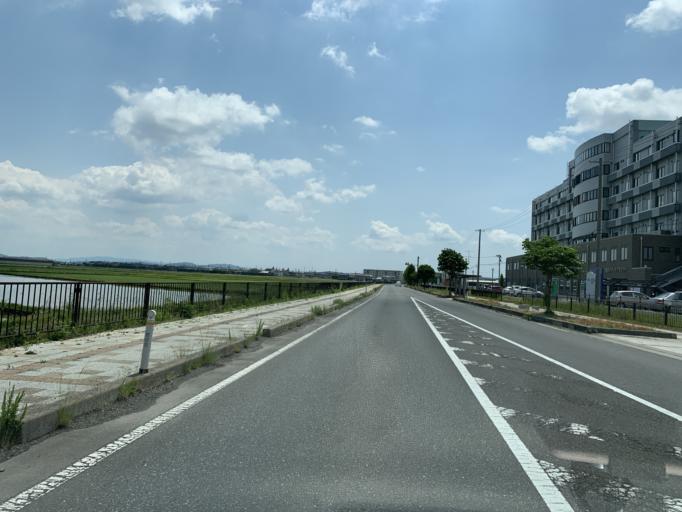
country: JP
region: Miyagi
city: Kogota
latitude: 38.5155
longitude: 141.0616
